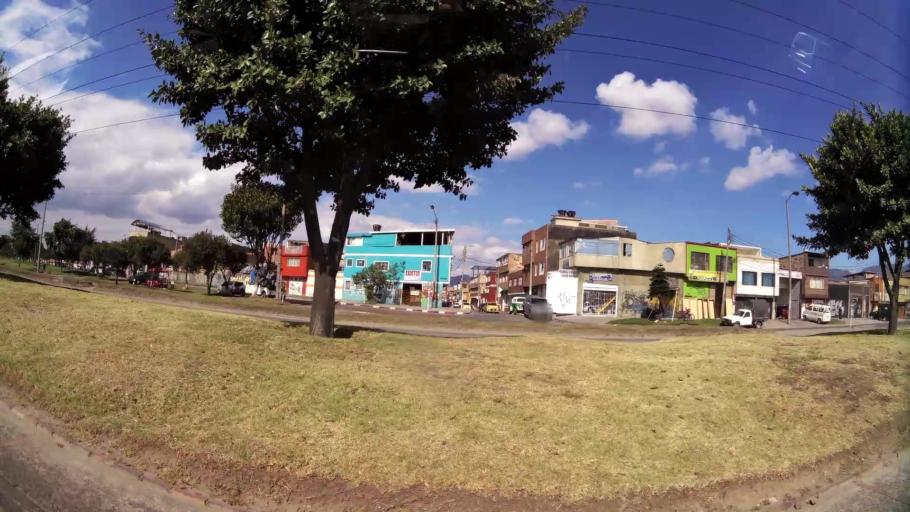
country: CO
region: Bogota D.C.
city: Bogota
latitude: 4.5819
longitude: -74.1430
